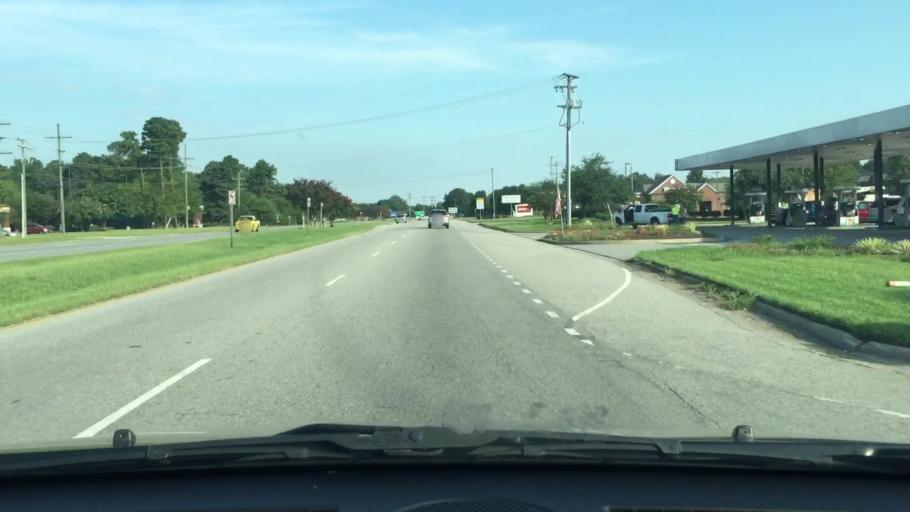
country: US
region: Virginia
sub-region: Isle of Wight County
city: Smithfield
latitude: 36.9571
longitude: -76.6024
